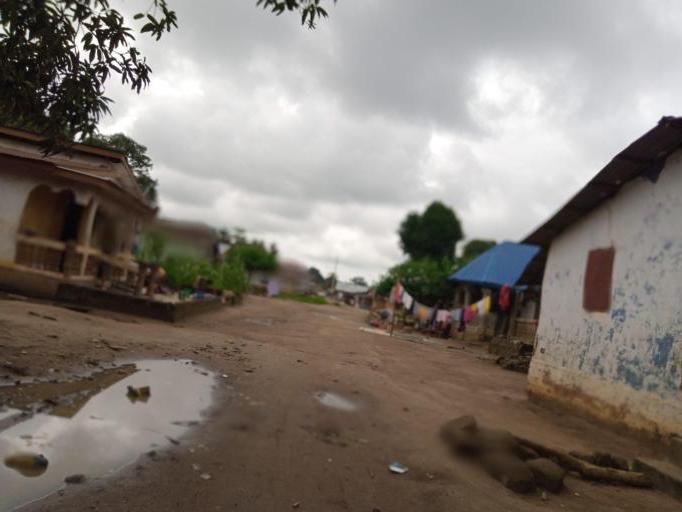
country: SL
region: Northern Province
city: Masoyila
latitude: 8.5897
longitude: -13.2003
